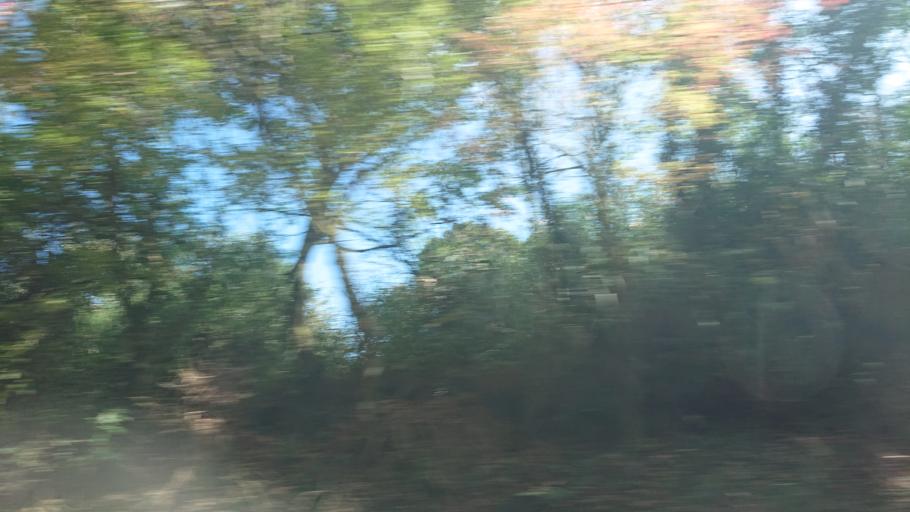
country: TW
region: Taiwan
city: Lugu
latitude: 23.5003
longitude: 120.8019
